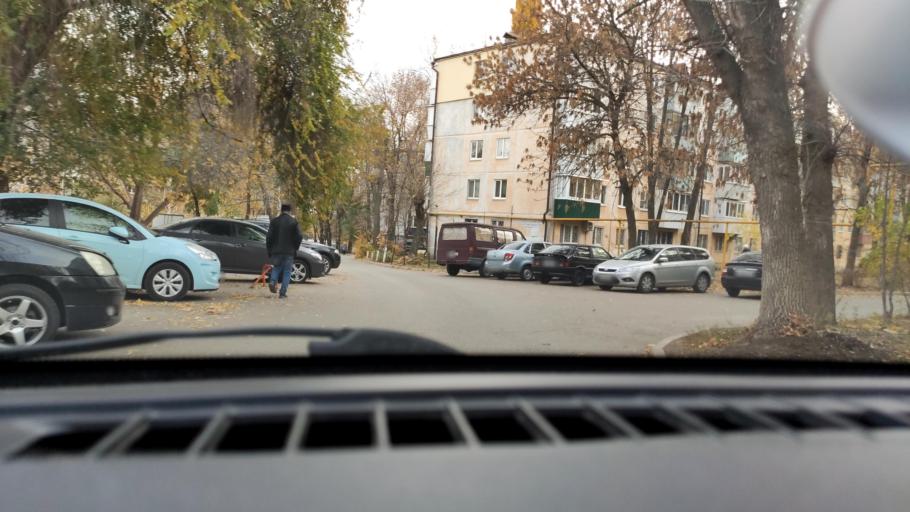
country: RU
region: Samara
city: Samara
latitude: 53.2325
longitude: 50.2177
